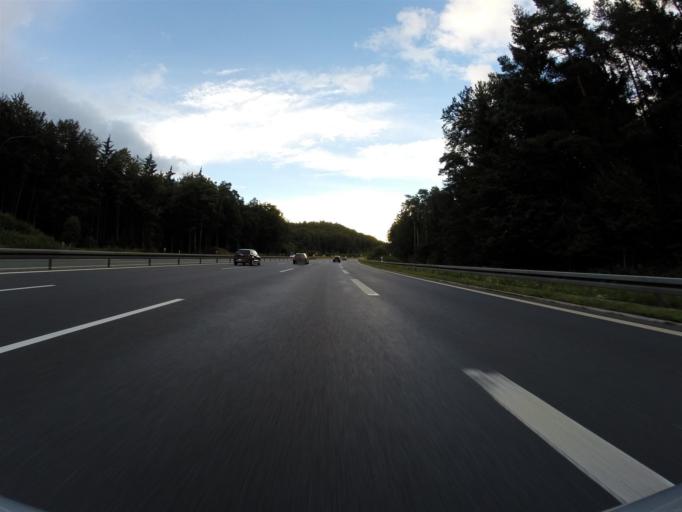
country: DE
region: Bavaria
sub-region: Regierungsbezirk Mittelfranken
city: Velden
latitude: 49.6482
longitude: 11.4376
